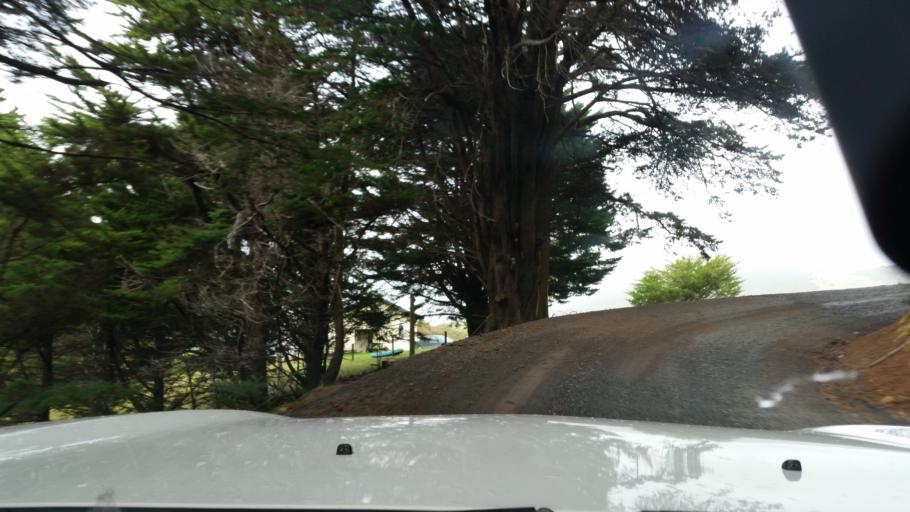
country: NZ
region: Northland
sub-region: Whangarei
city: Ruakaka
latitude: -35.7776
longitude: 174.5427
